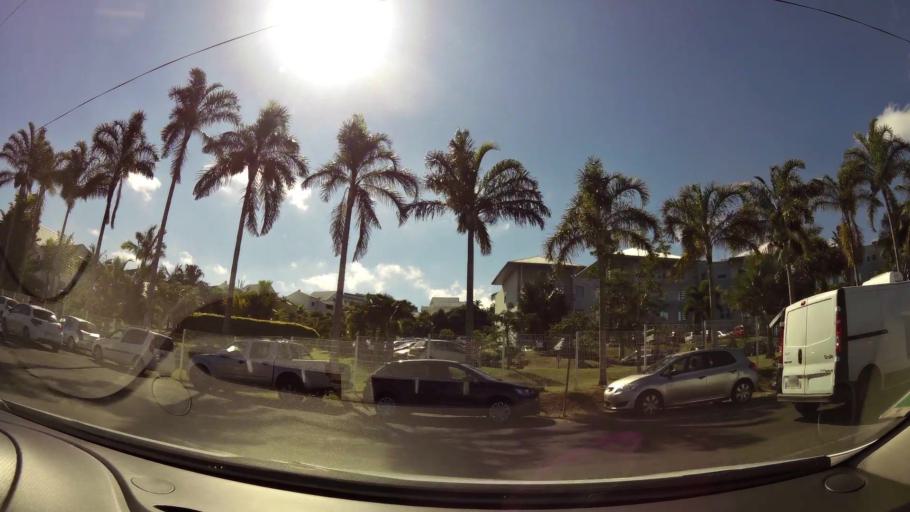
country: RE
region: Reunion
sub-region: Reunion
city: Le Tampon
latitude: -21.2749
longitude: 55.5071
